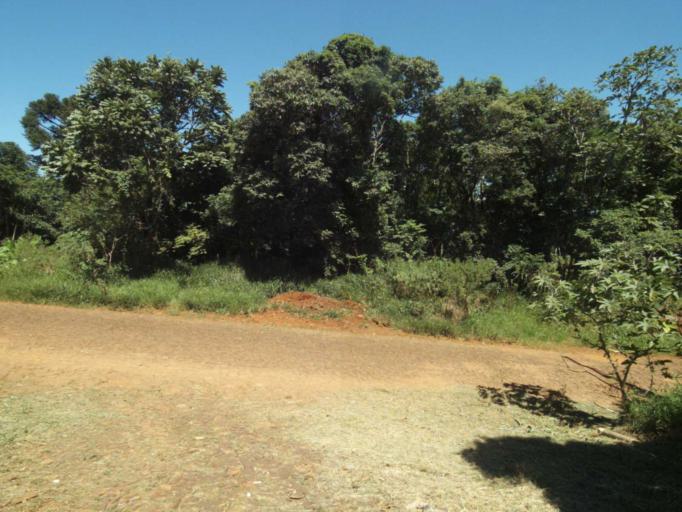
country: BR
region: Parana
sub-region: Laranjeiras Do Sul
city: Laranjeiras do Sul
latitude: -25.3900
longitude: -52.2140
